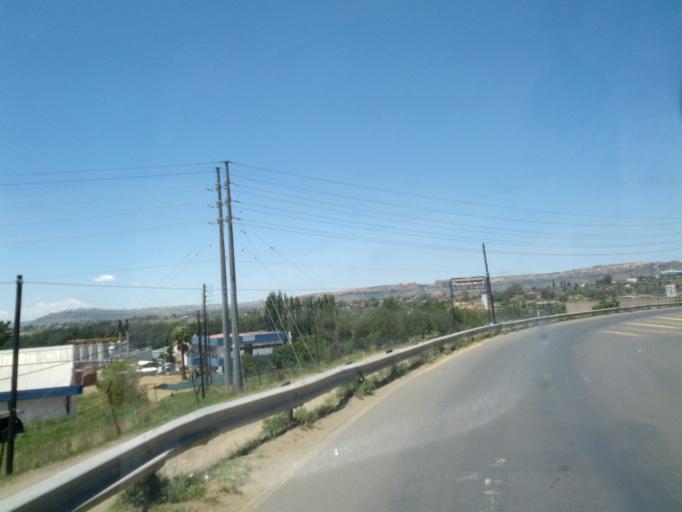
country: LS
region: Maseru
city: Maseru
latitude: -29.2986
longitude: 27.4798
